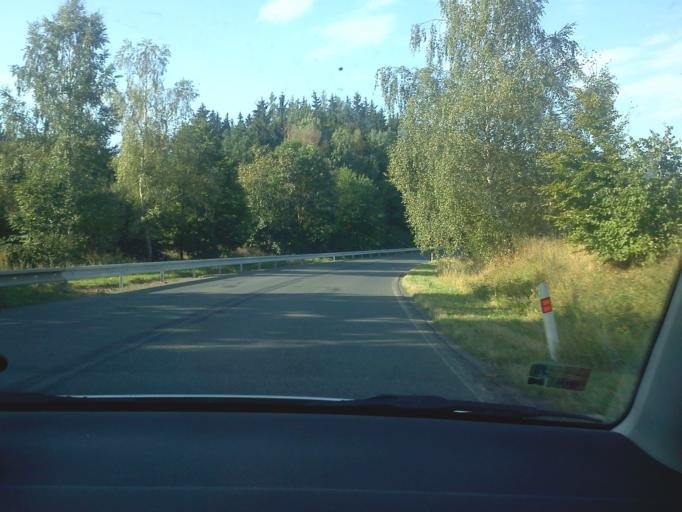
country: CZ
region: Plzensky
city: Zbiroh
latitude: 49.8366
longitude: 13.8112
